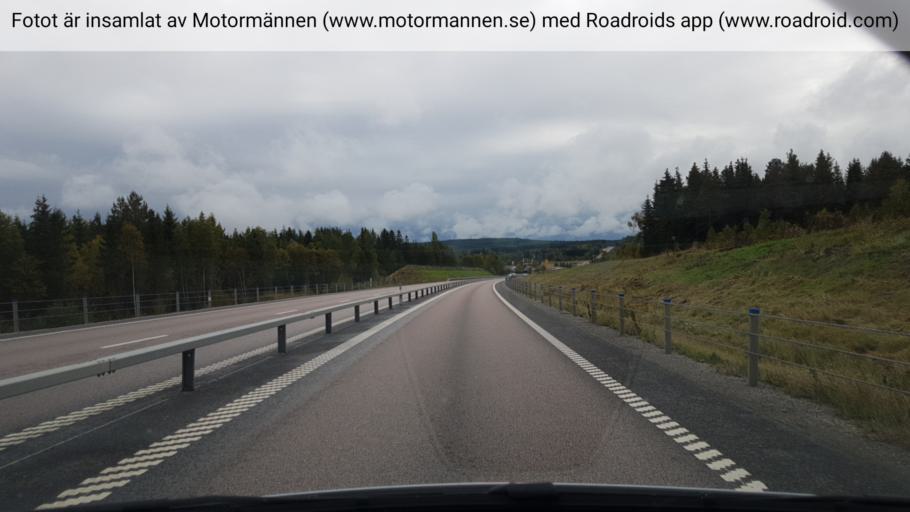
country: SE
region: Vaesternorrland
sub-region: Sundsvalls Kommun
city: Njurundabommen
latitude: 62.2559
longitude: 17.3695
